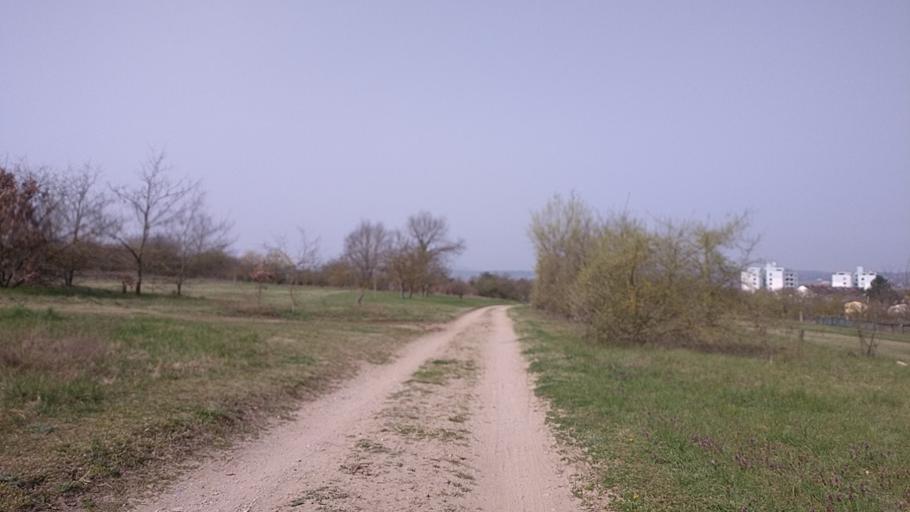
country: DE
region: Rheinland-Pfalz
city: Ingelheim am Rhein
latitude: 49.9675
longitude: 8.0367
